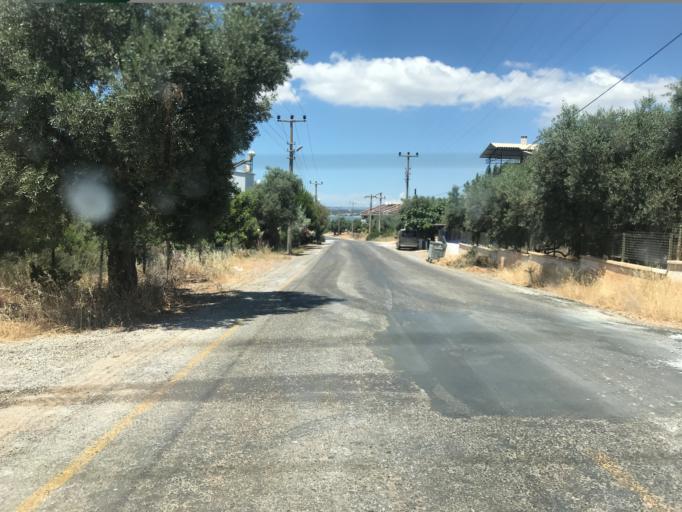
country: TR
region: Aydin
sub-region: Didim
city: Didim
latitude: 37.4000
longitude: 27.4359
